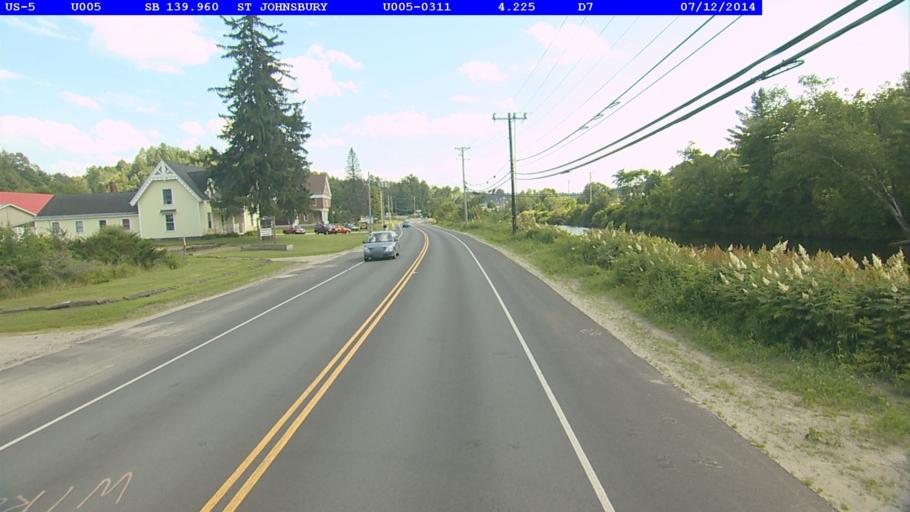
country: US
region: Vermont
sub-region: Caledonia County
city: St Johnsbury
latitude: 44.4521
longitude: -72.0163
